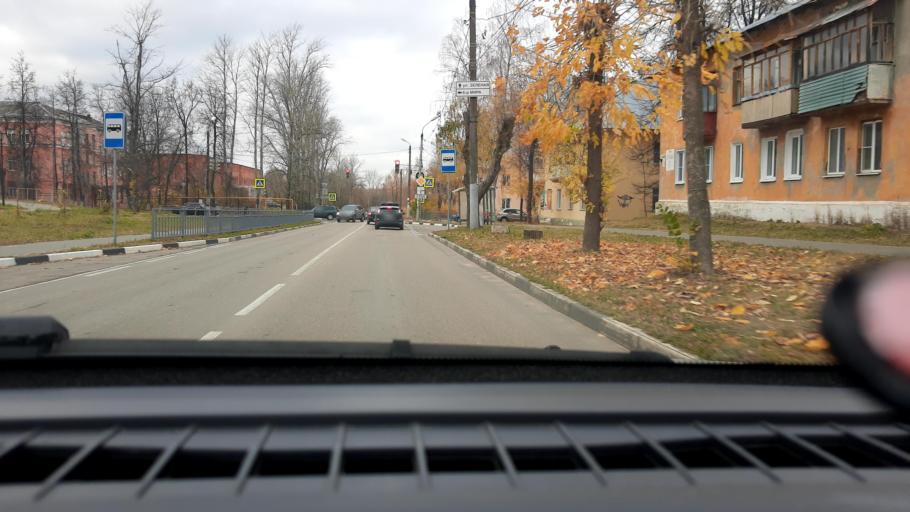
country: RU
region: Nizjnij Novgorod
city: Kstovo
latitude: 56.1523
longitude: 44.1968
